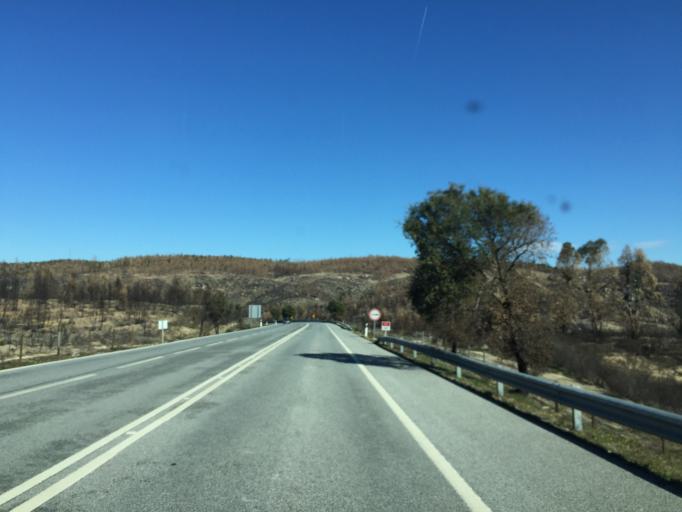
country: PT
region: Portalegre
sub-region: Nisa
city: Nisa
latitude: 39.5118
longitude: -7.7693
